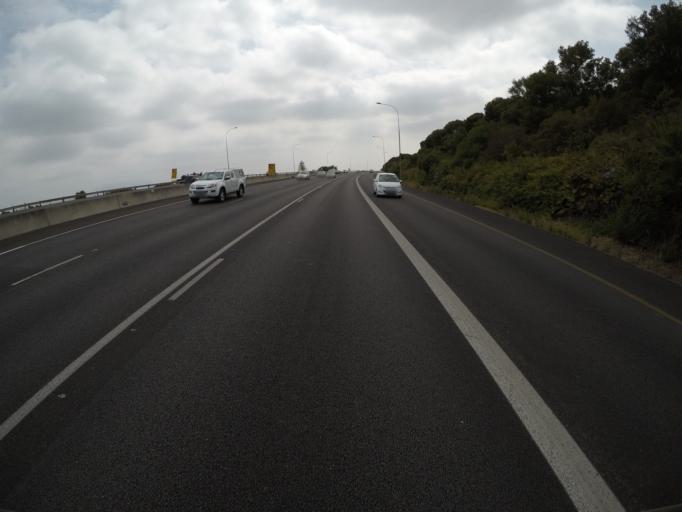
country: ZA
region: Western Cape
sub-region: City of Cape Town
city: Sunset Beach
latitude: -33.8893
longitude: 18.6021
